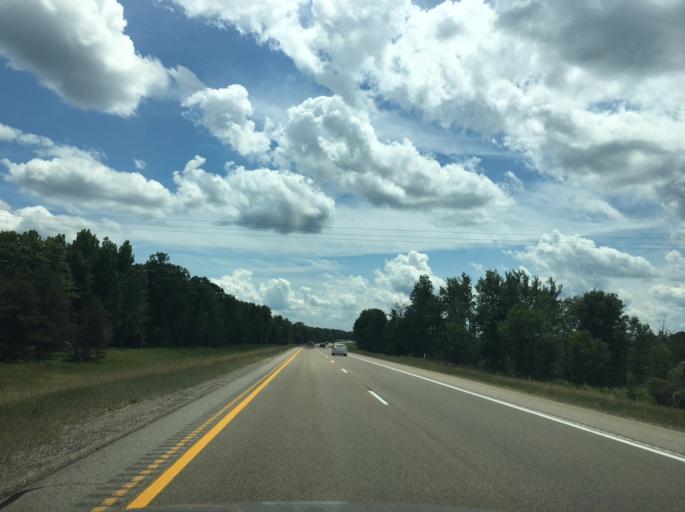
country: US
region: Michigan
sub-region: Crawford County
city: Grayling
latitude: 44.5699
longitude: -84.7090
